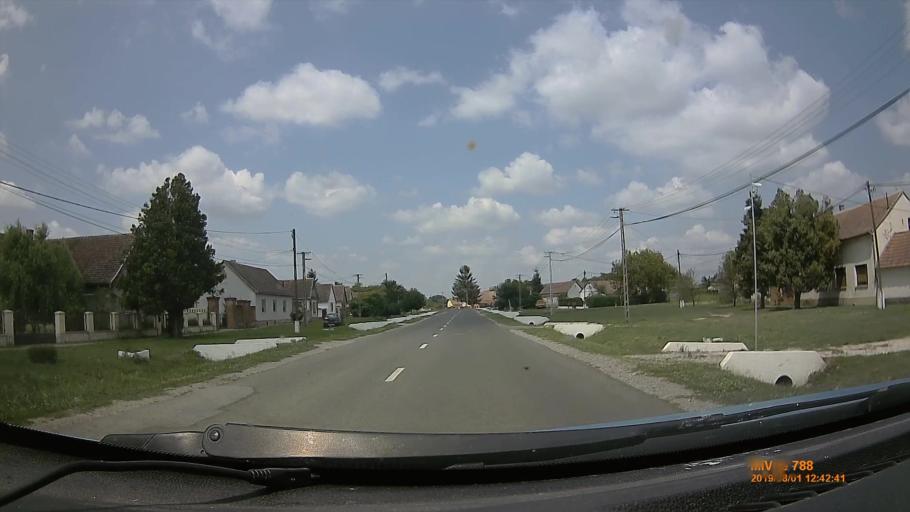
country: HU
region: Baranya
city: Harkany
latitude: 45.8367
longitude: 18.1618
